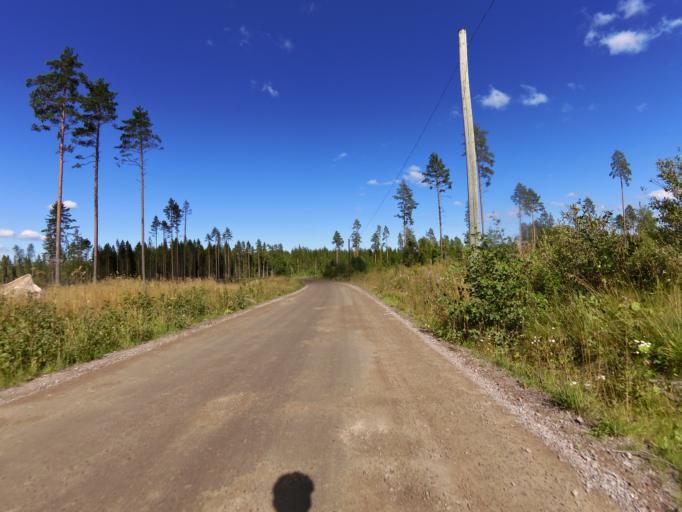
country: SE
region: Gaevleborg
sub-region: Hofors Kommun
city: Hofors
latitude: 60.5153
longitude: 16.3233
